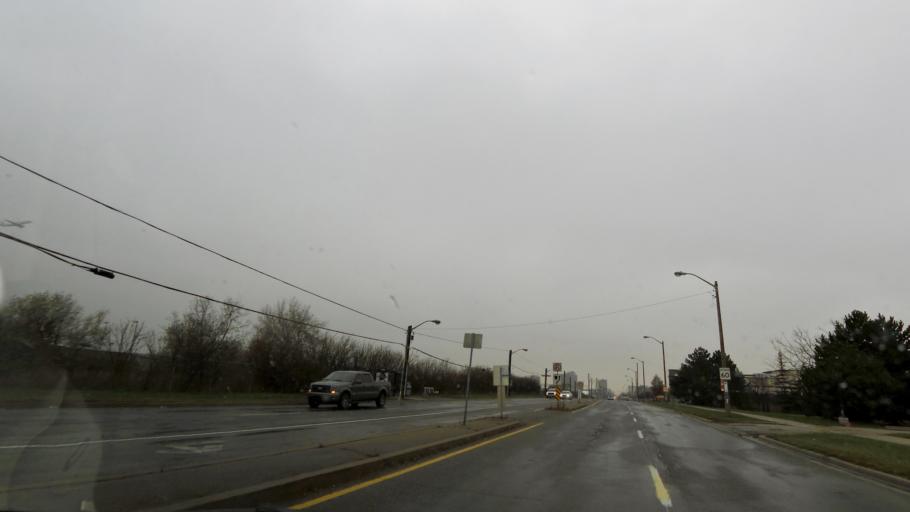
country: CA
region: Ontario
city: Etobicoke
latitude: 43.6770
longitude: -79.5911
